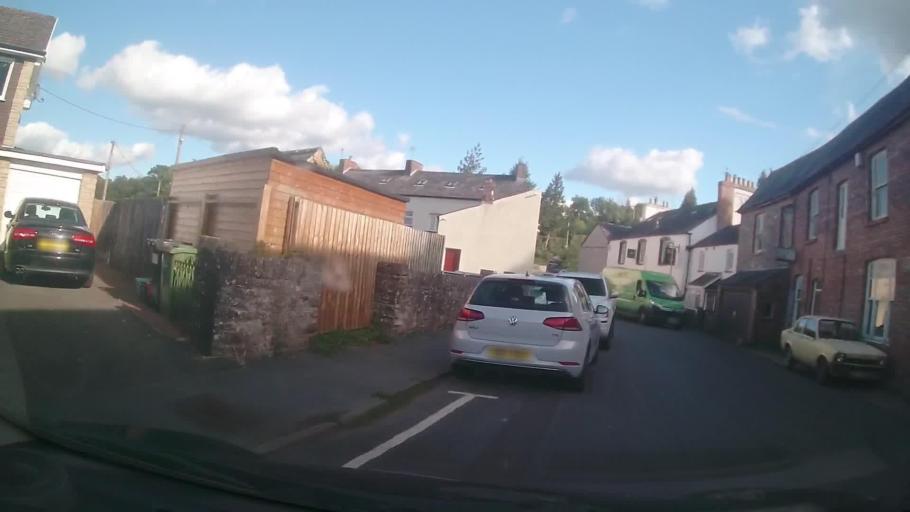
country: GB
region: Wales
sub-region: Sir Powys
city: Brecon
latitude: 51.8953
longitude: -3.2892
